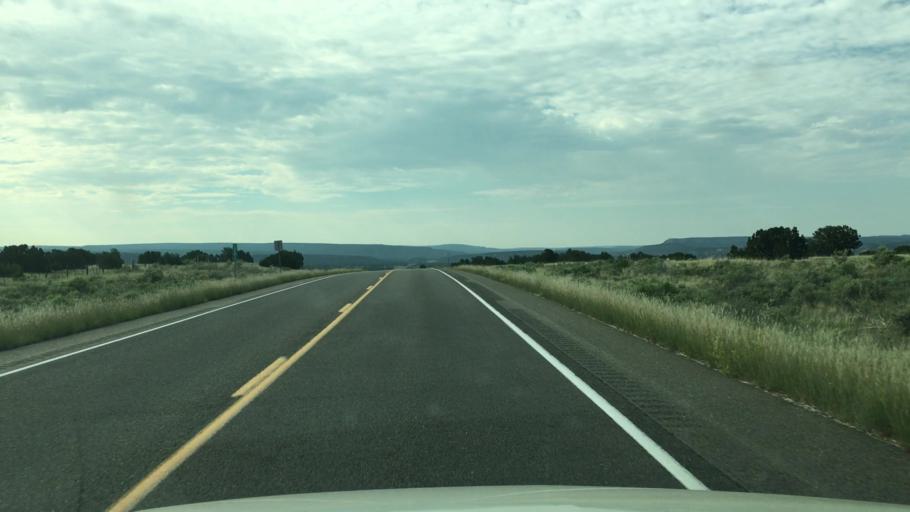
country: US
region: New Mexico
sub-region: Santa Fe County
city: Eldorado at Santa Fe
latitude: 35.4278
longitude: -105.8776
